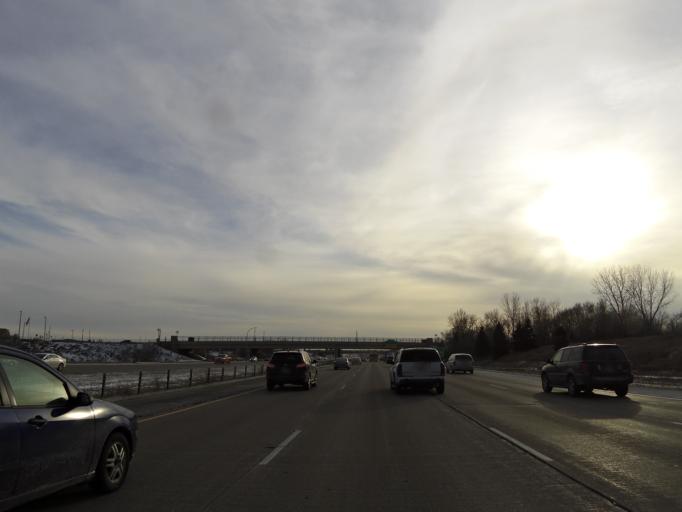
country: US
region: Minnesota
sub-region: Dakota County
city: Eagan
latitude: 44.8396
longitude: -93.1607
